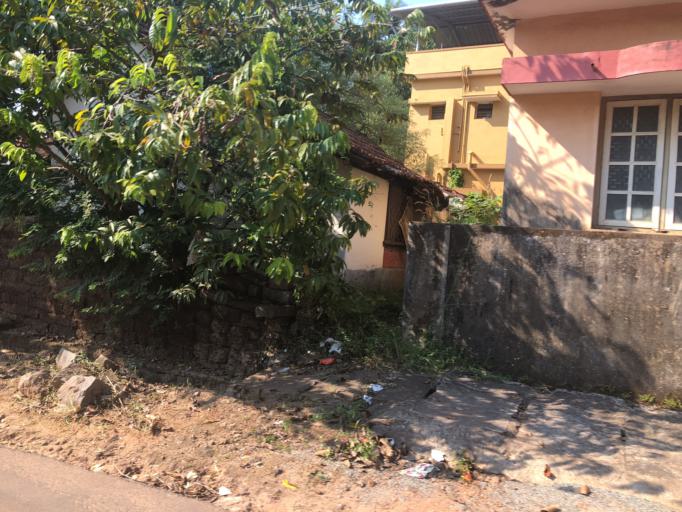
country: IN
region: Karnataka
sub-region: Dakshina Kannada
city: Mangalore
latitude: 12.8899
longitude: 74.8267
